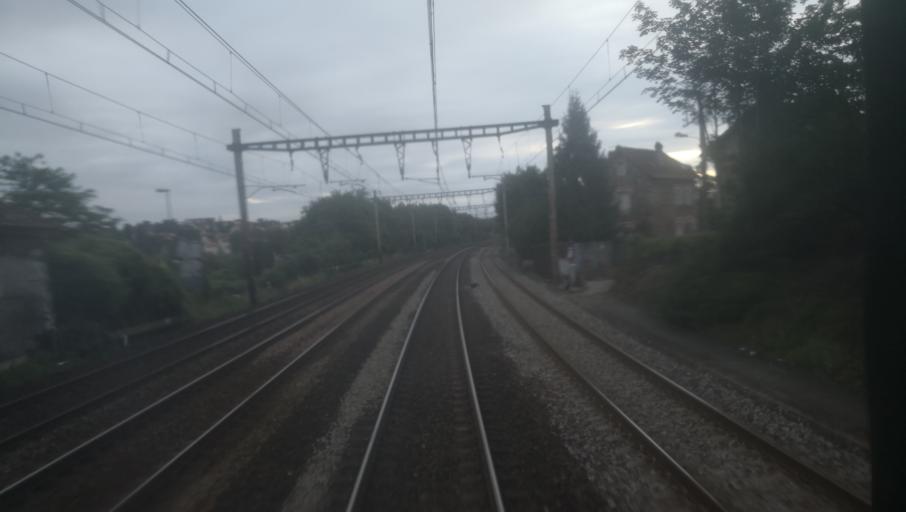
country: FR
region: Ile-de-France
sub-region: Departement de l'Essonne
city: Villemoisson-sur-Orge
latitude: 48.6662
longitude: 2.3248
